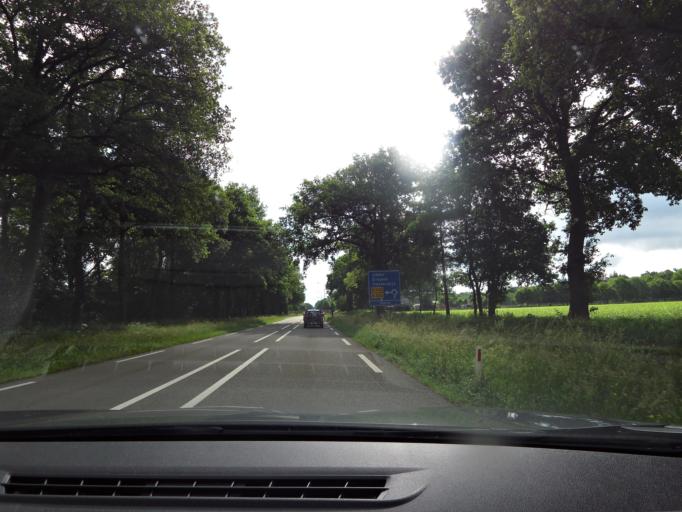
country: NL
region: Gelderland
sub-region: Gemeente Apeldoorn
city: Uddel
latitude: 52.2209
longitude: 5.7742
